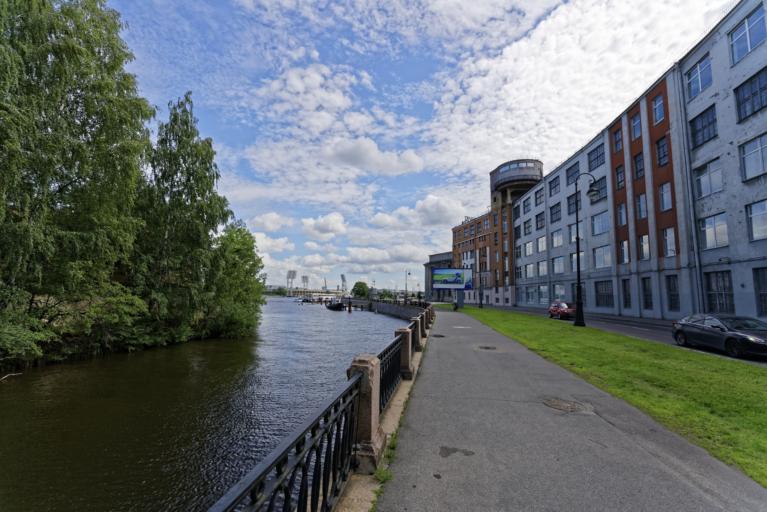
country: RU
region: St.-Petersburg
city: Vasyl'evsky Ostrov
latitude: 59.9498
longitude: 30.2721
